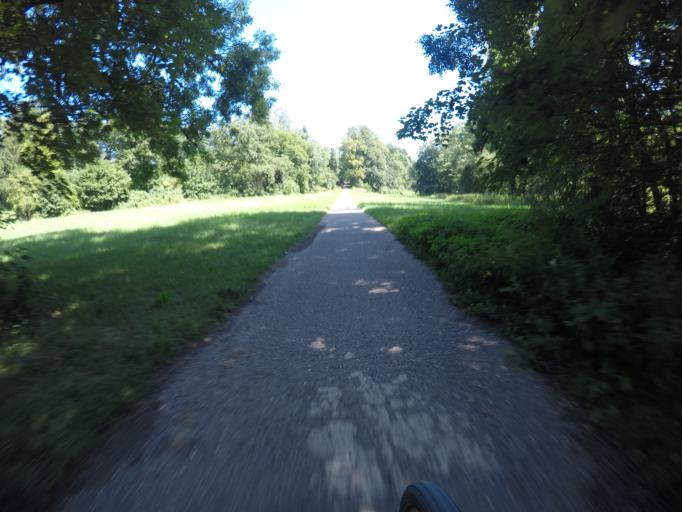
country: DE
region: Baden-Wuerttemberg
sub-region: Regierungsbezirk Stuttgart
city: Leinfelden-Echterdingen
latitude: 48.7097
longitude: 9.1834
